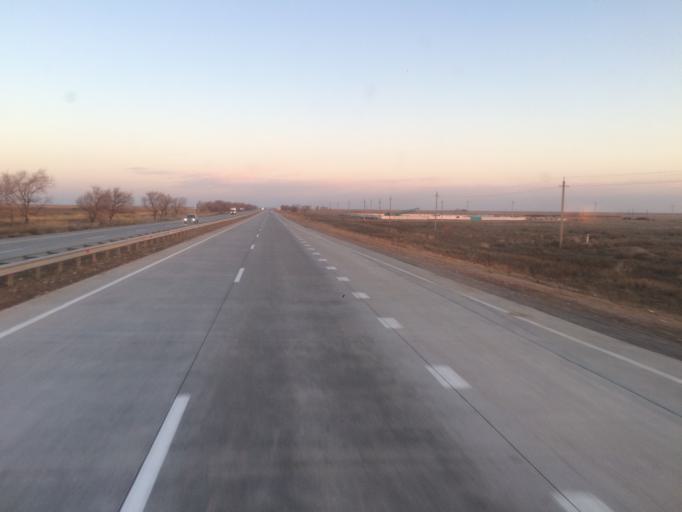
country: KZ
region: Ongtustik Qazaqstan
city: Bayaldyr
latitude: 43.0603
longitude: 68.6839
